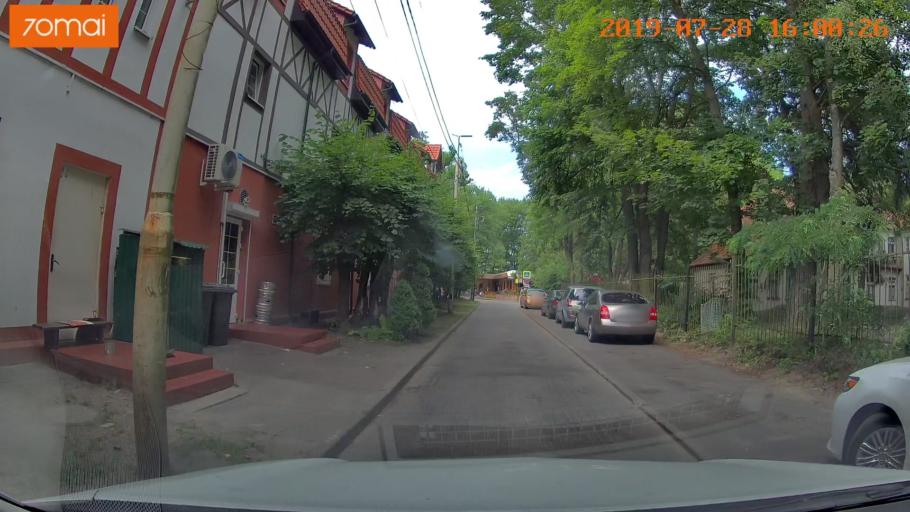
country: RU
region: Kaliningrad
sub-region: Gorod Svetlogorsk
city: Svetlogorsk
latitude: 54.9436
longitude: 20.1566
